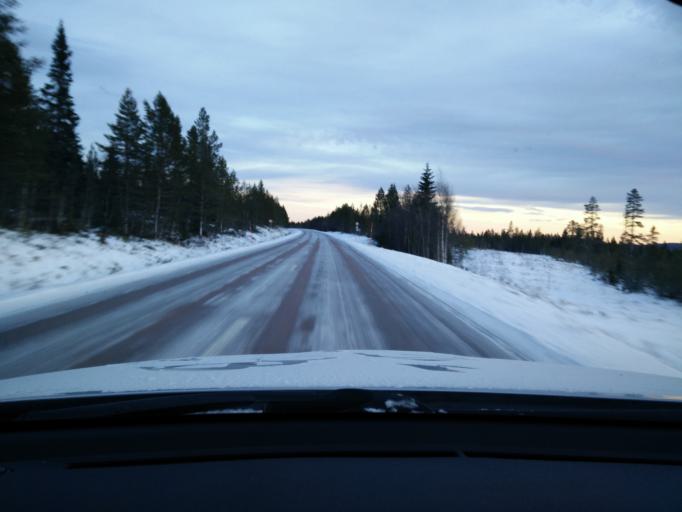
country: SE
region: Jaemtland
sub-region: Bergs Kommun
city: Hoverberg
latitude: 62.4771
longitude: 14.1398
